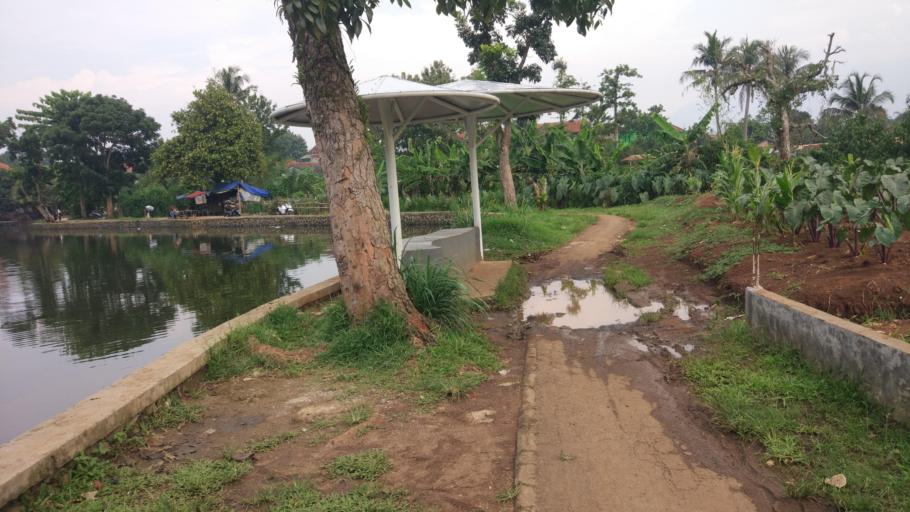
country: ID
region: West Java
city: Ciampea
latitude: -6.5531
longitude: 106.7468
